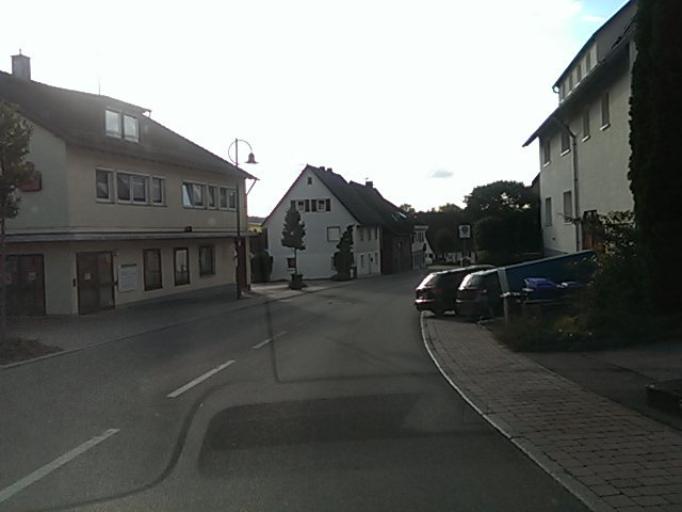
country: DE
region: Baden-Wuerttemberg
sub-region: Freiburg Region
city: Seedorf
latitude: 48.3000
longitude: 8.4886
